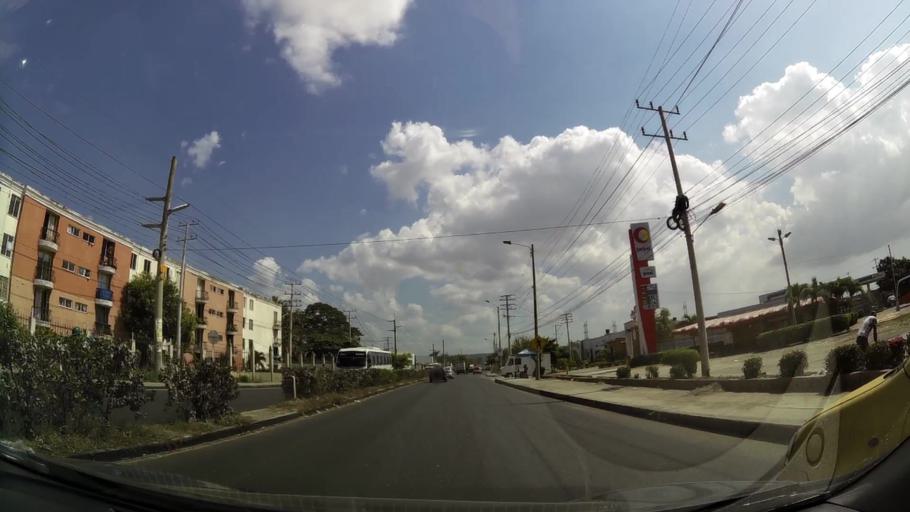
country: CO
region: Bolivar
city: Cartagena
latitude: 10.3812
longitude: -75.4647
